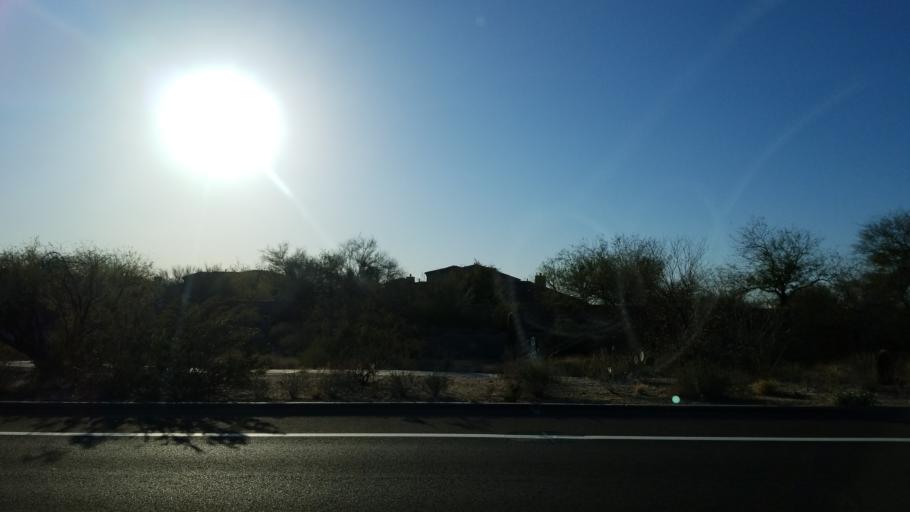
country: US
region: Arizona
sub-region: Maricopa County
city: Paradise Valley
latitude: 33.6691
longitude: -111.8907
